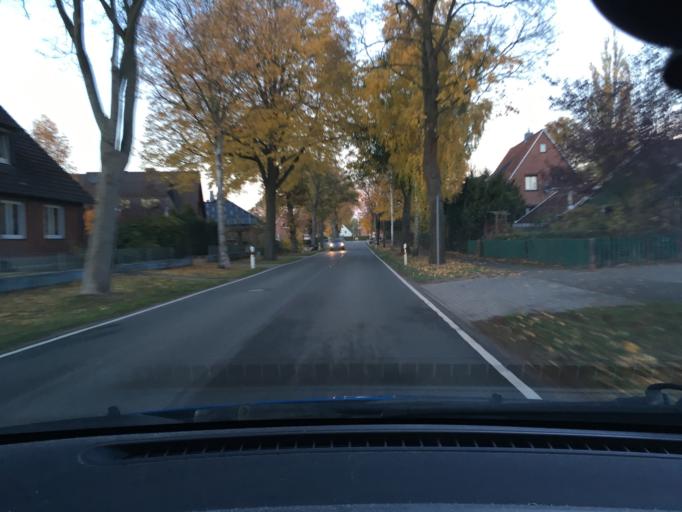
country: DE
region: Lower Saxony
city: Radbruch
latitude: 53.3348
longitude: 10.3037
